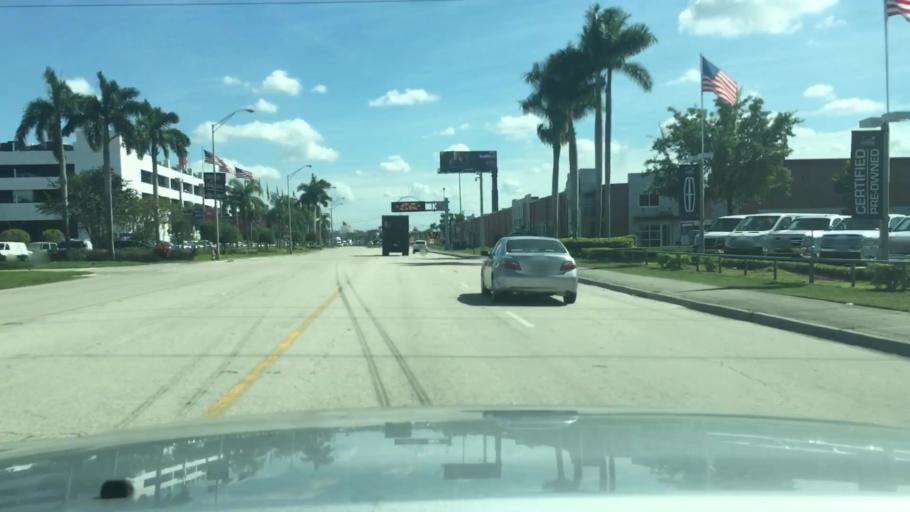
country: US
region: Florida
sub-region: Miami-Dade County
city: Fountainebleau
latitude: 25.7832
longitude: -80.3416
